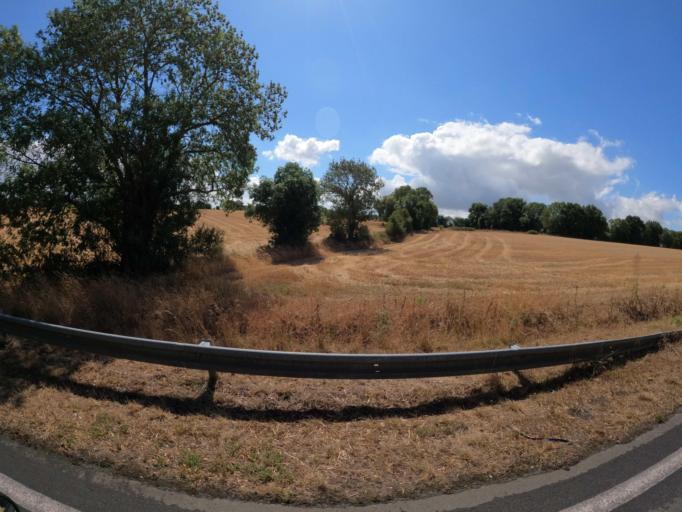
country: FR
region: Pays de la Loire
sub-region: Departement de Maine-et-Loire
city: Saint-Laurent-des-Autels
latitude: 47.2920
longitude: -1.1789
